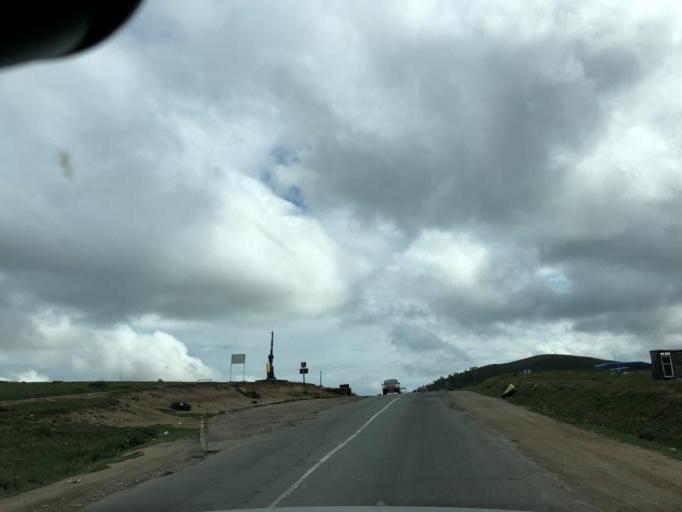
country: MN
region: Central Aimak
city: Ihsueuej
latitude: 48.1354
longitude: 106.4246
